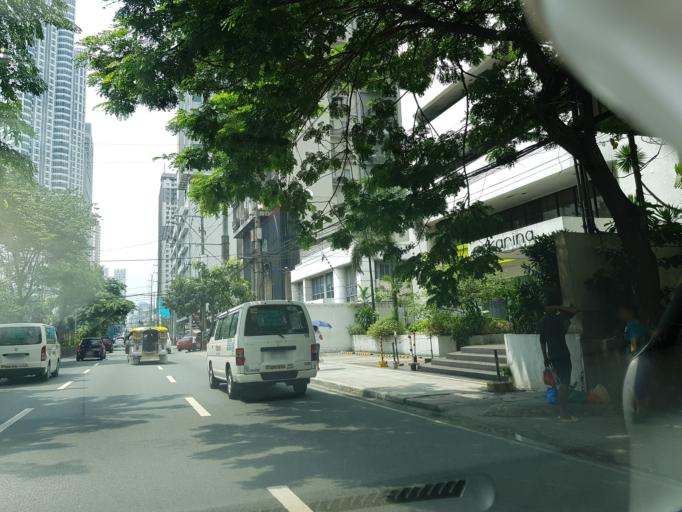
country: PH
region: Metro Manila
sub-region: Pasig
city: Pasig City
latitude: 14.5772
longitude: 121.0584
